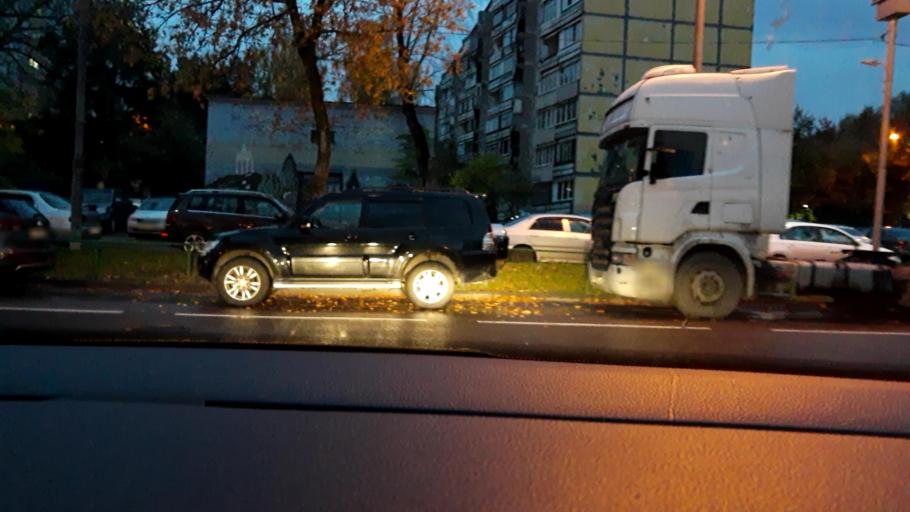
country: RU
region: Moscow
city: Vostochnyy
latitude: 55.8220
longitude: 37.8729
